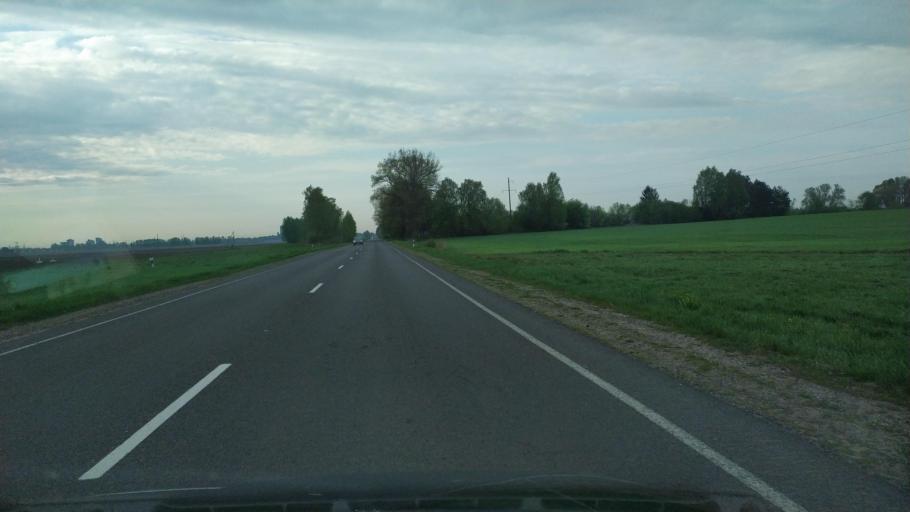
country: BY
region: Brest
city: Zhabinka
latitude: 52.2231
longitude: 23.9907
